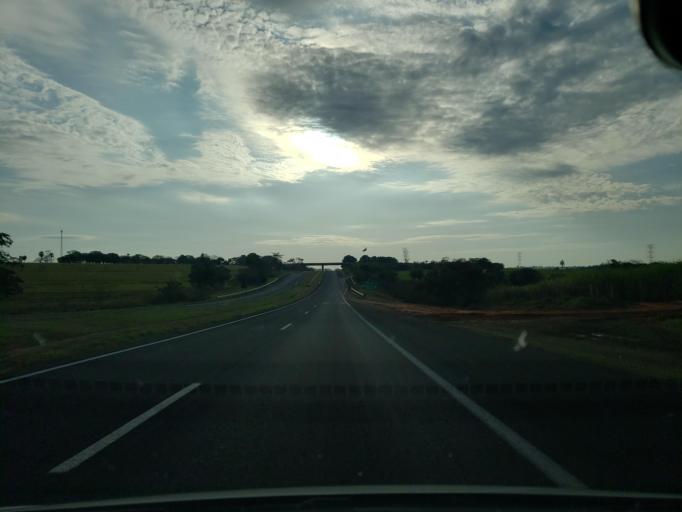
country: BR
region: Sao Paulo
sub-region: Mirandopolis
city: Mirandopolis
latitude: -21.0892
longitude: -51.0580
